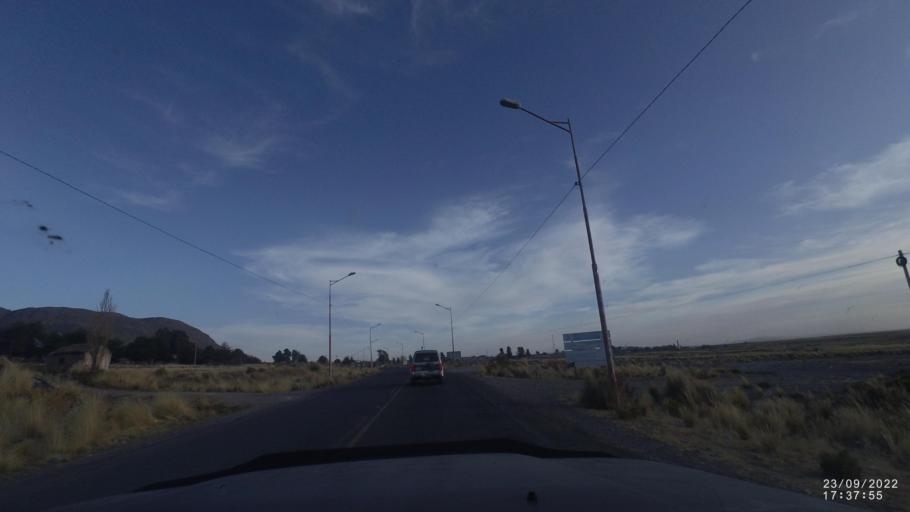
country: BO
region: Oruro
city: Challapata
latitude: -19.0008
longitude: -66.7773
